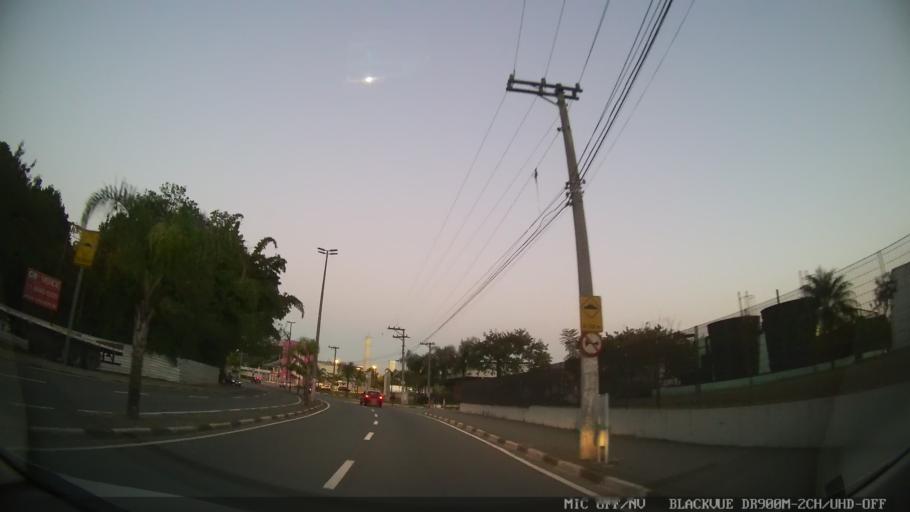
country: BR
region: Sao Paulo
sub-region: Barueri
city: Barueri
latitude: -23.4964
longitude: -46.8716
